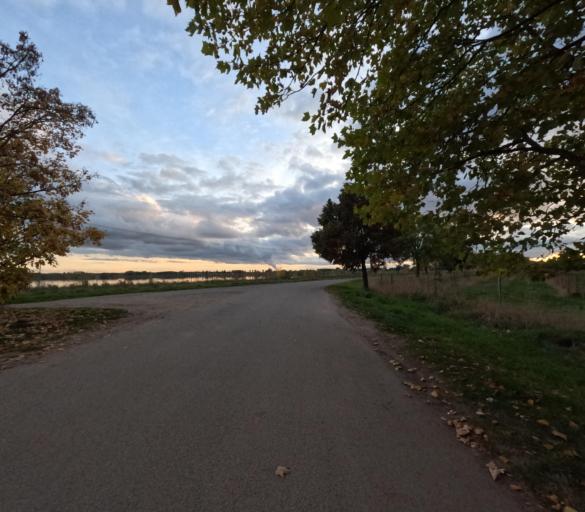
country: DE
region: Saxony
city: Borsdorf
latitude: 51.3101
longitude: 12.5260
